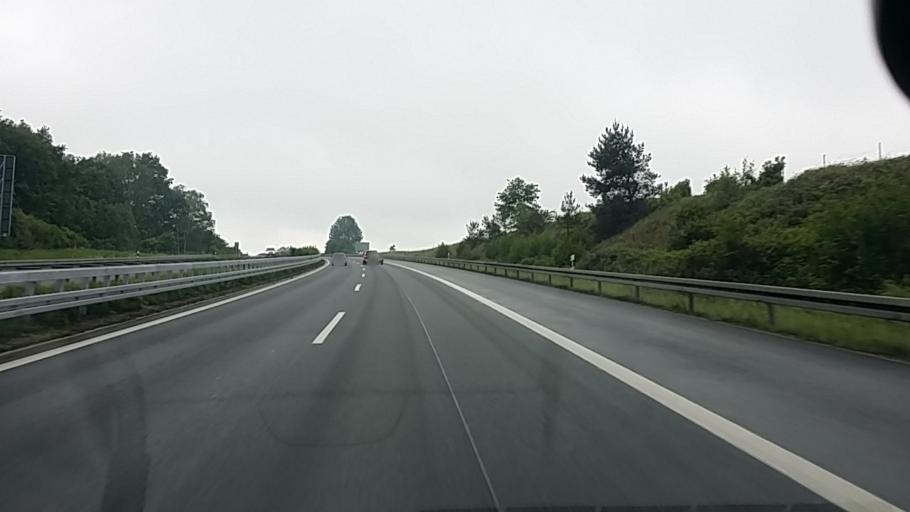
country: DE
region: Saxony
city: Ottendorf-Okrilla
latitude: 51.1719
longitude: 13.8127
